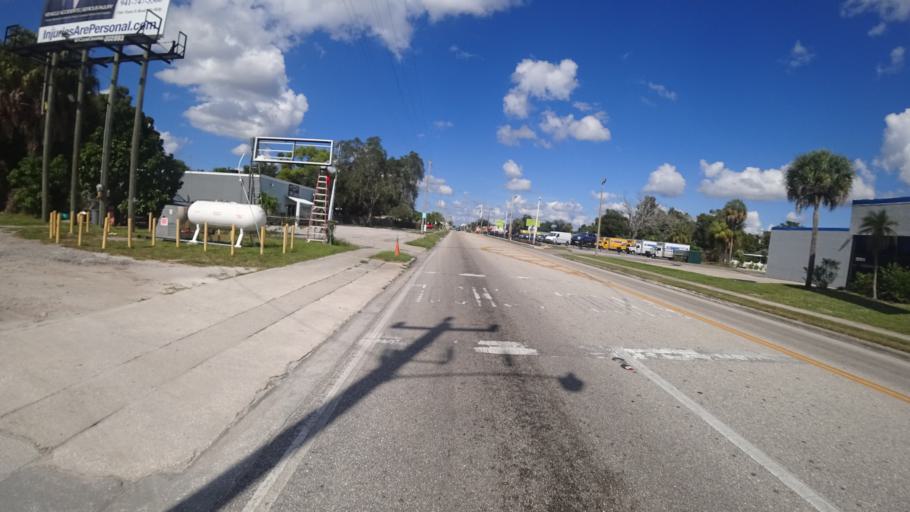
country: US
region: Florida
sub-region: Manatee County
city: West Samoset
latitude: 27.4744
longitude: -82.5713
